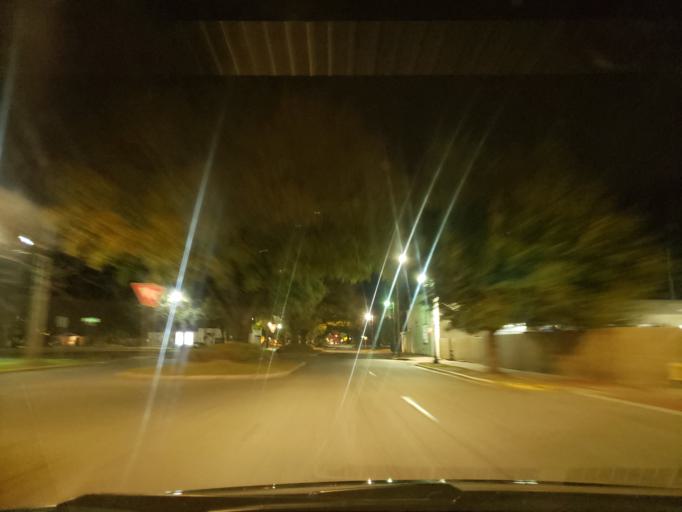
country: US
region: Georgia
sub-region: Chatham County
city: Savannah
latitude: 32.0505
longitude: -81.1082
